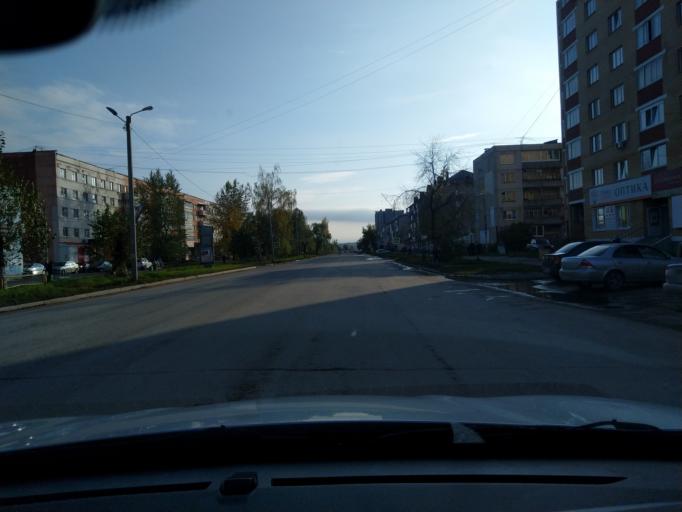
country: RU
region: Perm
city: Dobryanka
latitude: 58.4677
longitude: 56.4038
